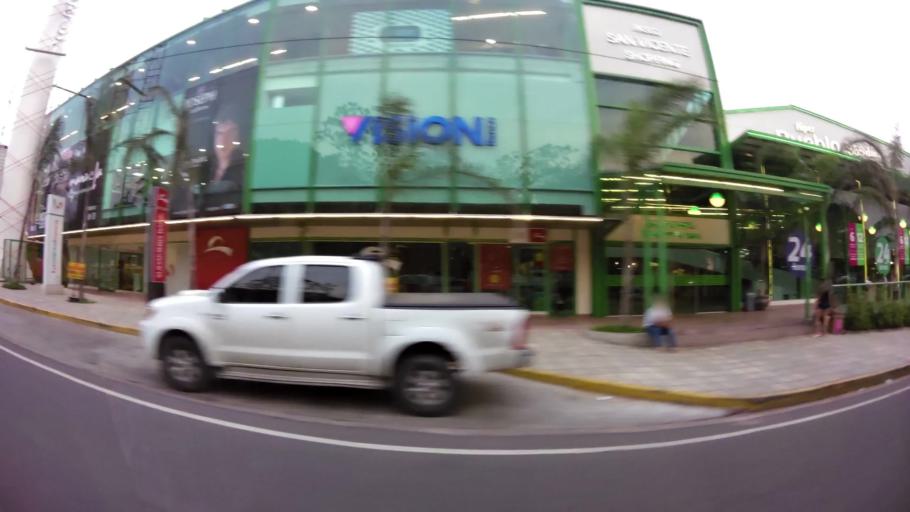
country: PY
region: Asuncion
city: Asuncion
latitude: -25.3173
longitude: -57.6200
